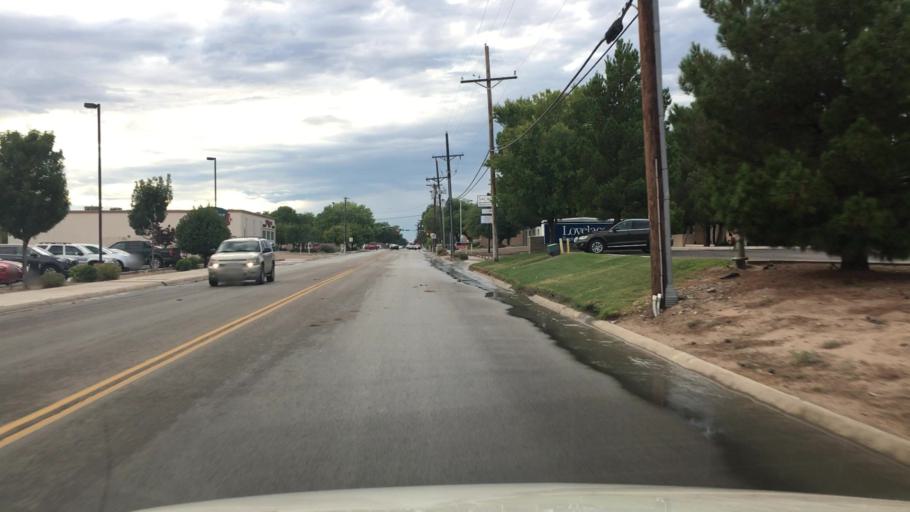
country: US
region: New Mexico
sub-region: Chaves County
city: Roswell
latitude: 33.4160
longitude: -104.5203
